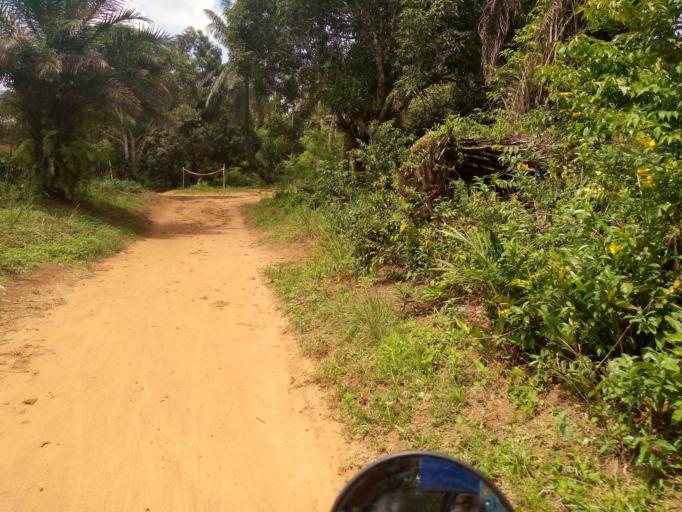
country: SL
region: Western Area
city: Waterloo
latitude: 8.3584
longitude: -12.9259
